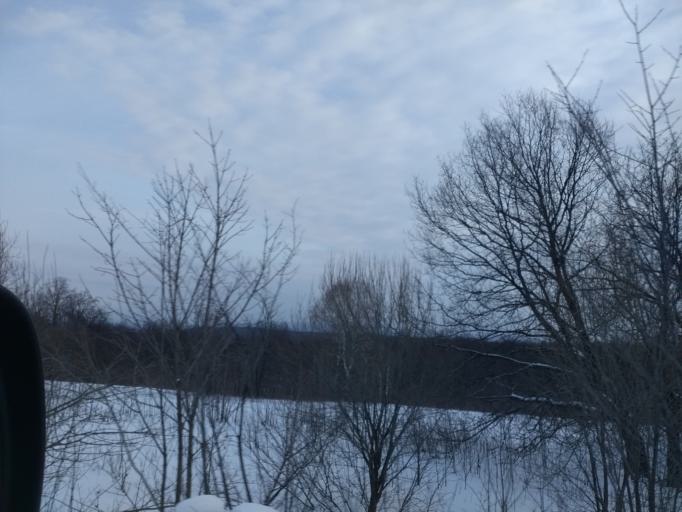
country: RU
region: Bashkortostan
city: Kudeyevskiy
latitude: 54.7280
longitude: 56.6108
